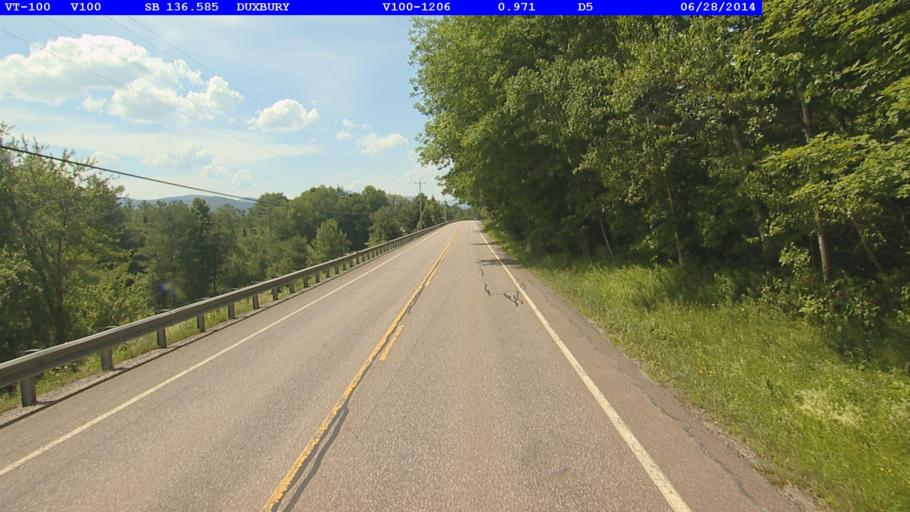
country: US
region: Vermont
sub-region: Washington County
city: Waterbury
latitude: 44.2604
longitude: -72.7879
